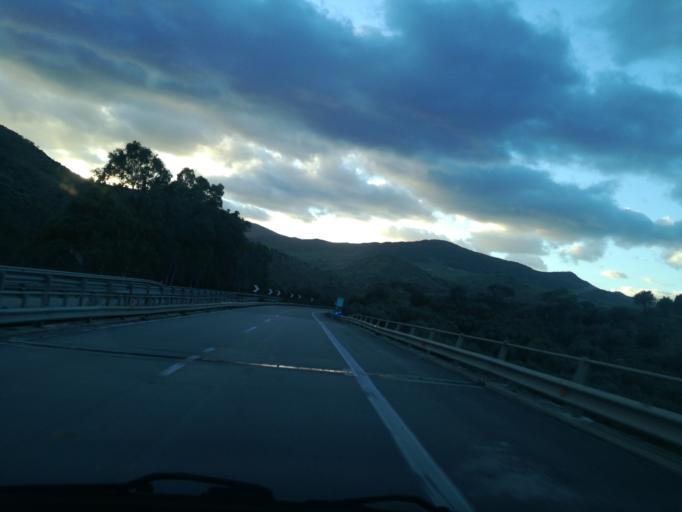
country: IT
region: Sicily
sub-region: Palermo
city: Scillato
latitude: 37.8637
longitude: 13.8825
